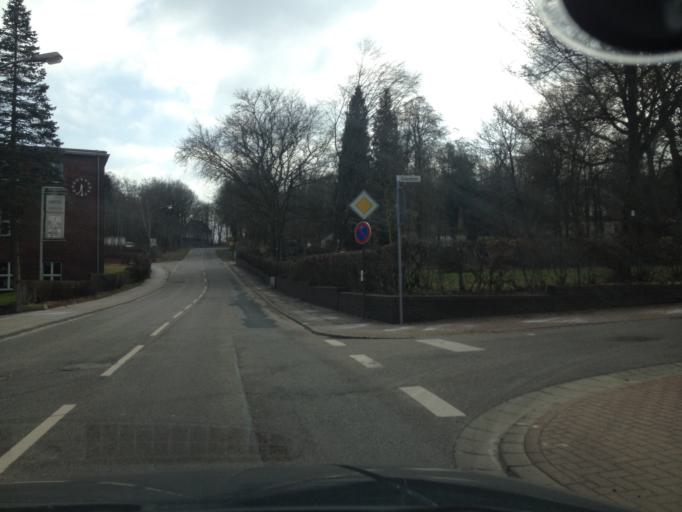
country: DE
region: Saarland
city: Friedrichsthal
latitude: 49.3499
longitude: 7.1119
